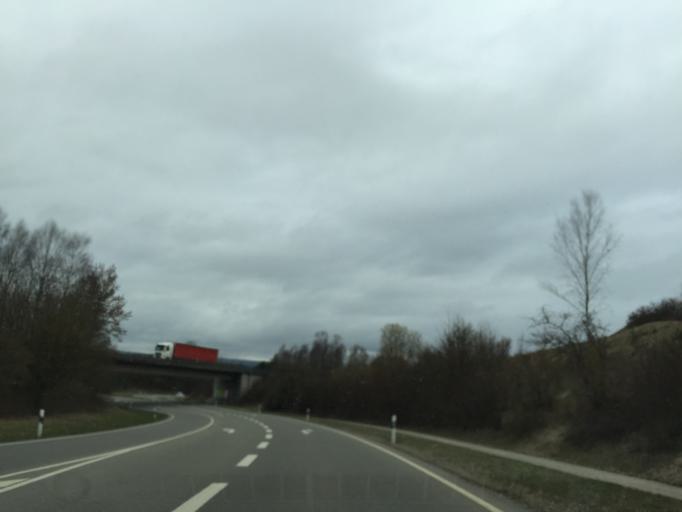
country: DE
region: Baden-Wuerttemberg
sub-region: Freiburg Region
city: Villingen-Schwenningen
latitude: 48.0491
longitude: 8.4767
